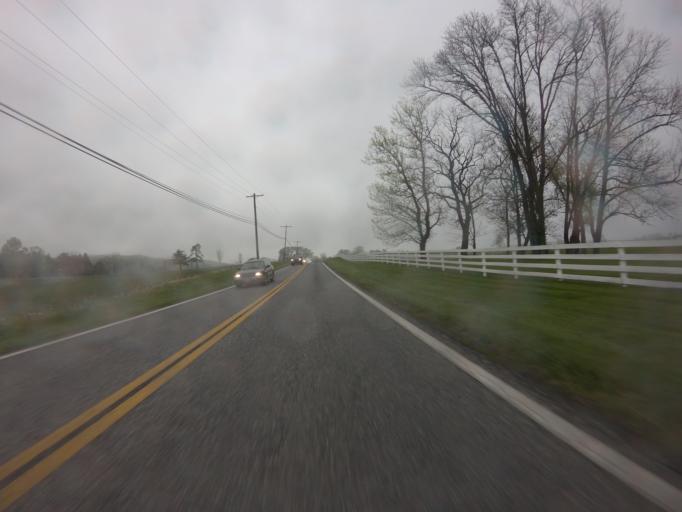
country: US
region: Maryland
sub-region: Baltimore County
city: Reisterstown
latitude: 39.4787
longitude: -76.7724
